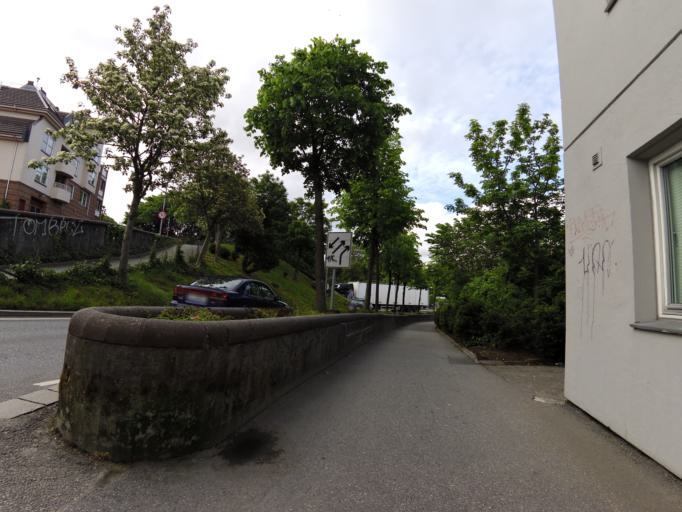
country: NO
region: Rogaland
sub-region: Stavanger
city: Stavanger
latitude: 58.9667
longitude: 5.7354
